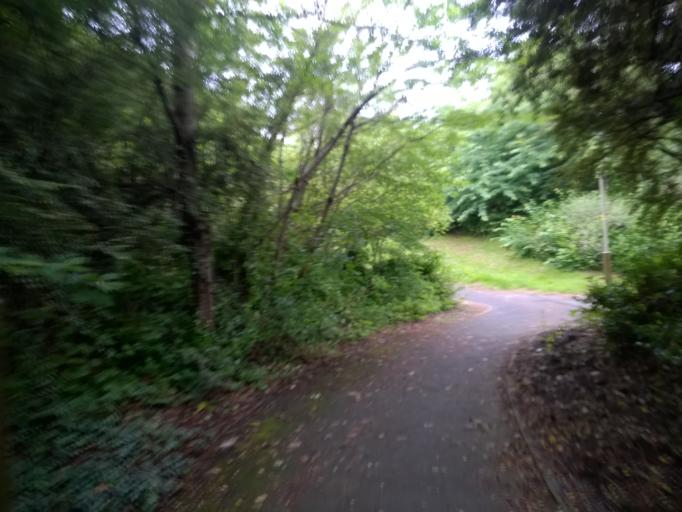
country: GB
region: England
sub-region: Leicestershire
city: Anstey
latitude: 52.6643
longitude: -1.1699
